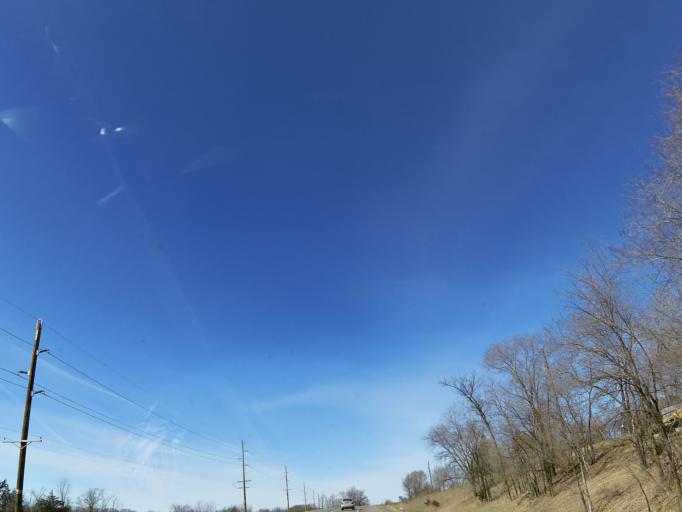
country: US
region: Minnesota
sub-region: Wright County
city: Annandale
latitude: 45.2679
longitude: -94.1511
